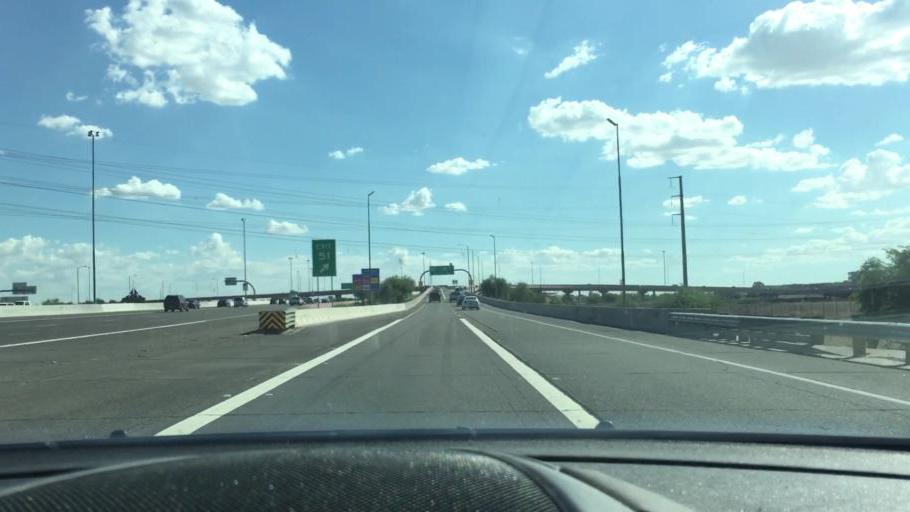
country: US
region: Arizona
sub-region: Maricopa County
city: Tempe
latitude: 33.4414
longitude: -111.8902
